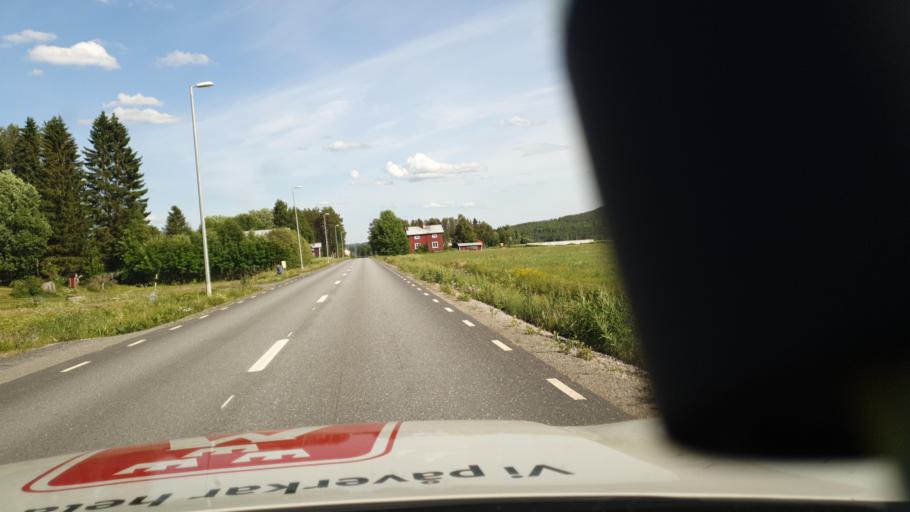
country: SE
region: Vaesterbotten
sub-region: Skelleftea Kommun
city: Forsbacka
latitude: 64.6892
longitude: 20.5112
